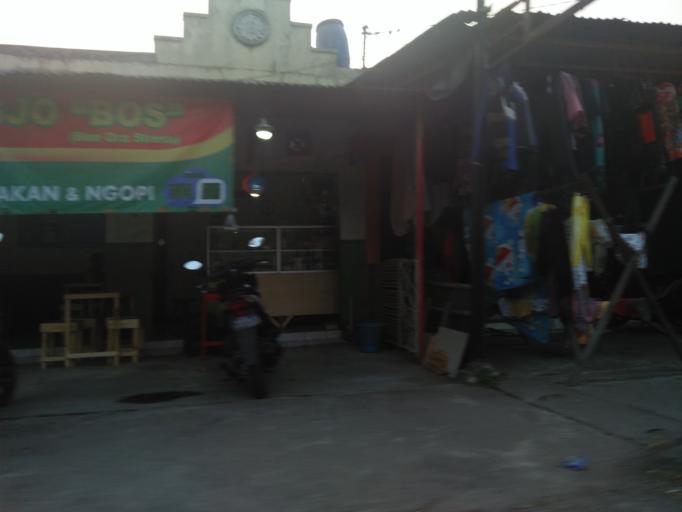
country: ID
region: Daerah Istimewa Yogyakarta
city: Sewon
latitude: -7.8501
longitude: 110.4102
